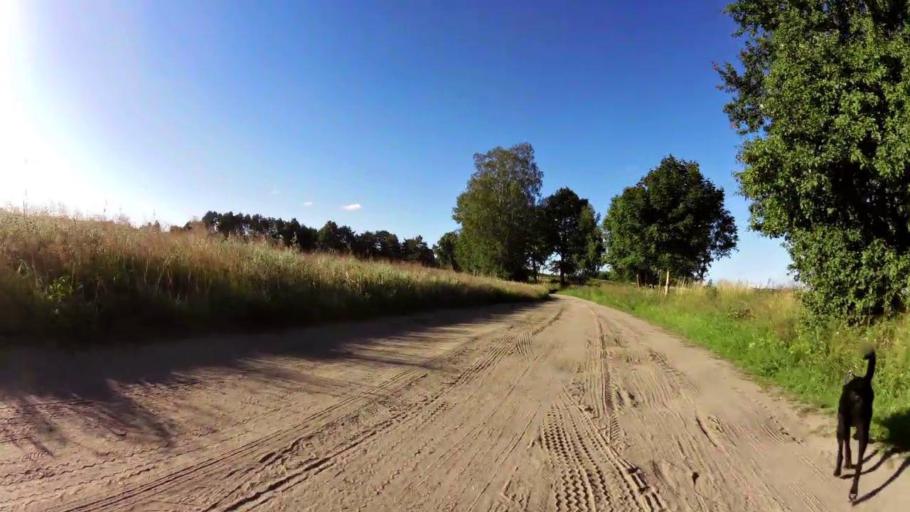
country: PL
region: West Pomeranian Voivodeship
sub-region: Powiat swidwinski
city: Swidwin
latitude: 53.7067
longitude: 15.8284
